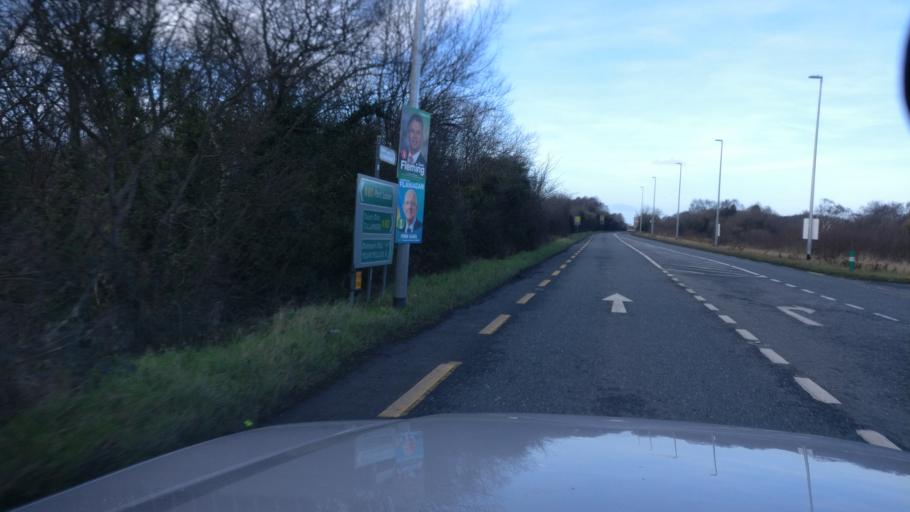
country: IE
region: Leinster
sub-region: Laois
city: Portlaoise
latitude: 53.0670
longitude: -7.3268
